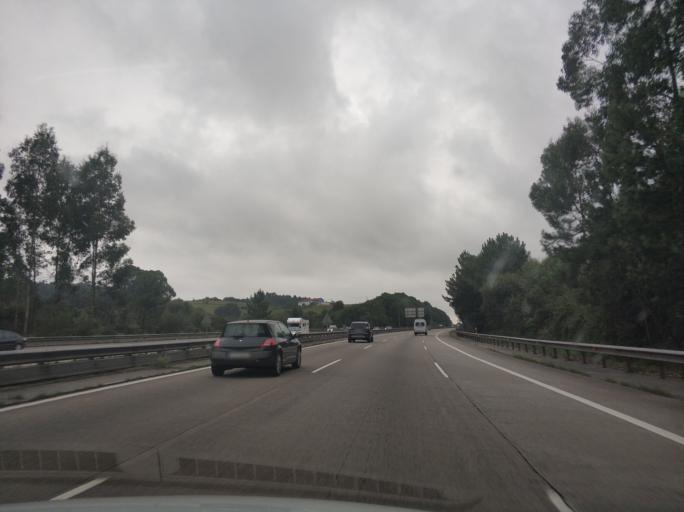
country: ES
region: Asturias
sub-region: Province of Asturias
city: Corvera de Asturias
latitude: 43.5046
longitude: -5.8034
